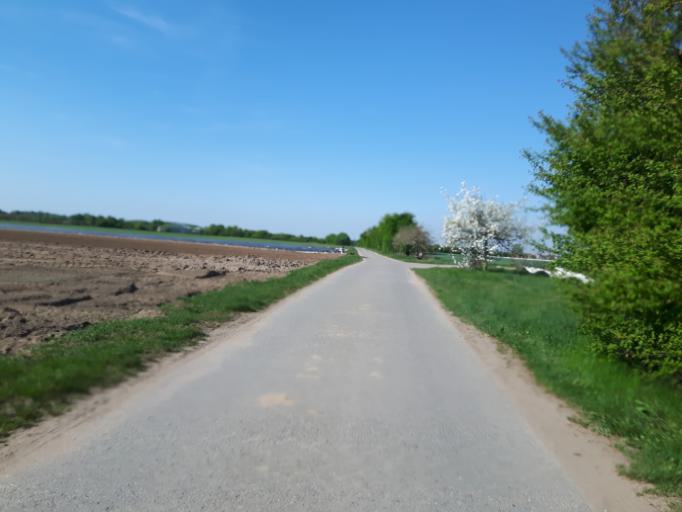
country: DE
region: Baden-Wuerttemberg
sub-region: Karlsruhe Region
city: Neulussheim
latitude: 49.2986
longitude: 8.5367
